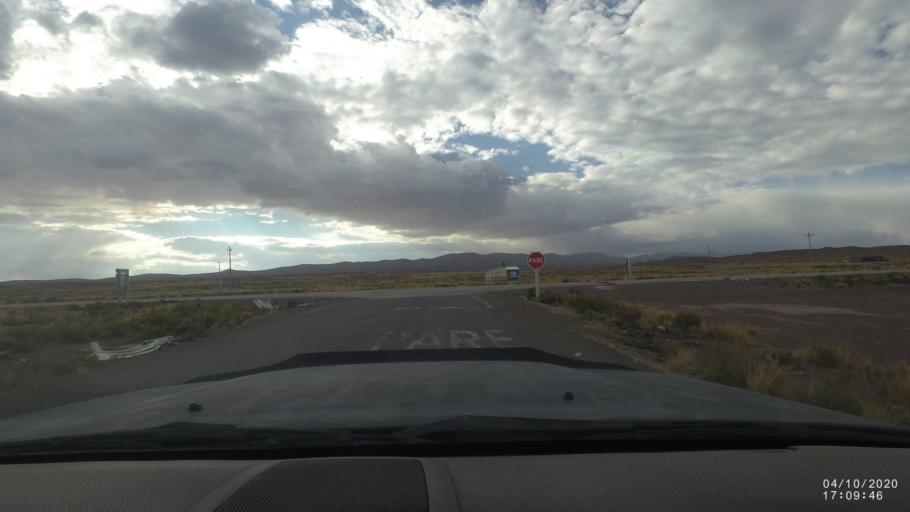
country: BO
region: Oruro
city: Oruro
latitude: -18.3369
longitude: -67.5876
